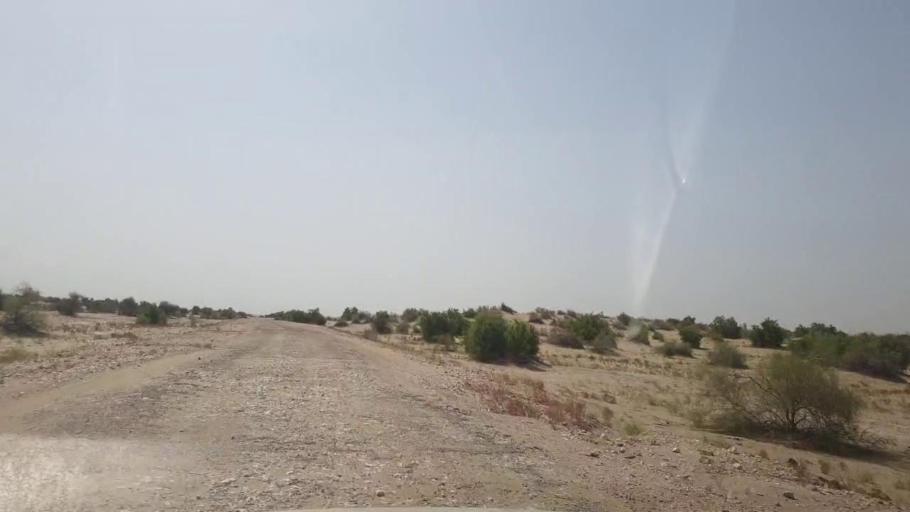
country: PK
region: Sindh
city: Rohri
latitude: 27.4355
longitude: 69.2472
